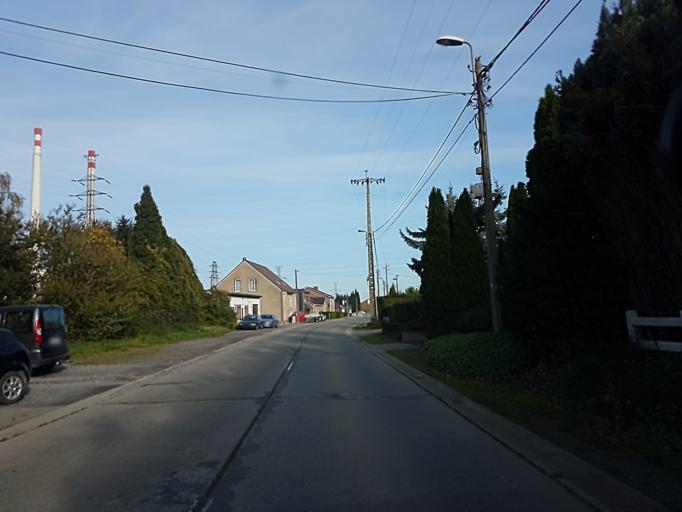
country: BE
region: Wallonia
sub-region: Province de Liege
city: Engis
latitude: 50.5813
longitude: 5.4149
